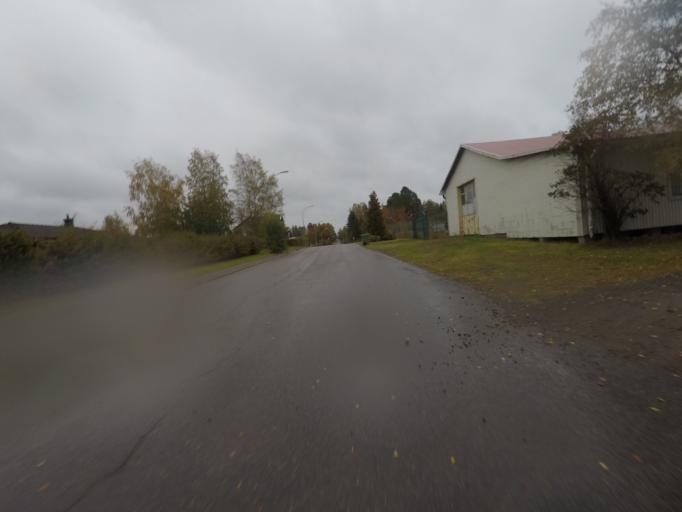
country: SE
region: OErebro
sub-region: Karlskoga Kommun
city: Karlskoga
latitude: 59.3079
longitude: 14.4719
